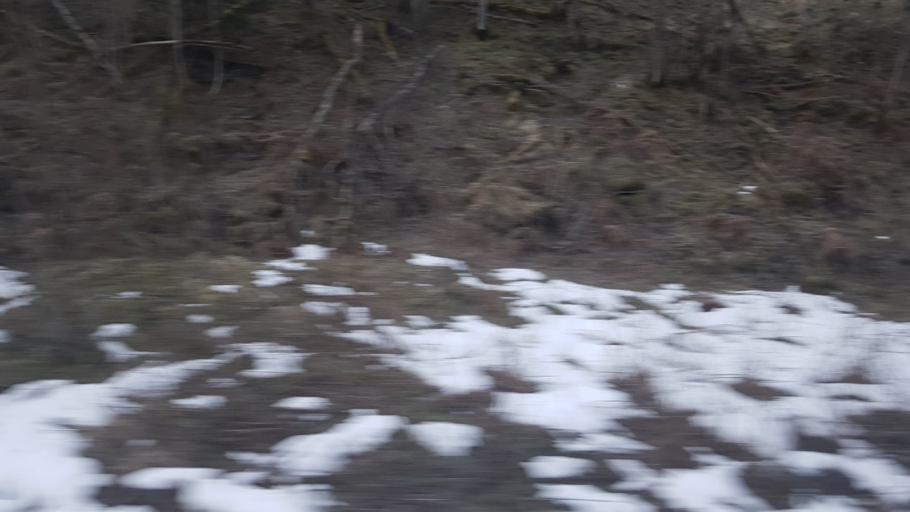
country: NO
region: Nord-Trondelag
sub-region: Stjordal
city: Stjordalshalsen
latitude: 63.5849
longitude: 11.0035
